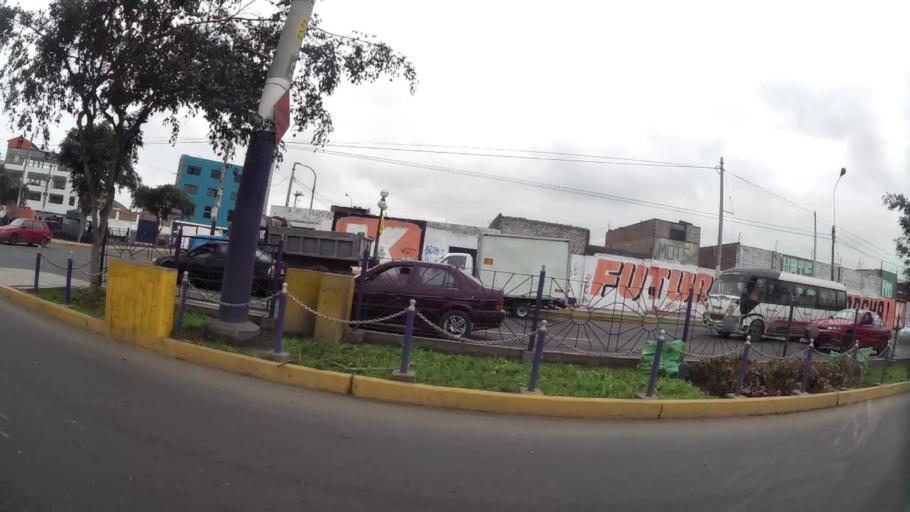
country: PE
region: Lima
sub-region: Lima
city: Surco
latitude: -12.1843
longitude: -77.0043
